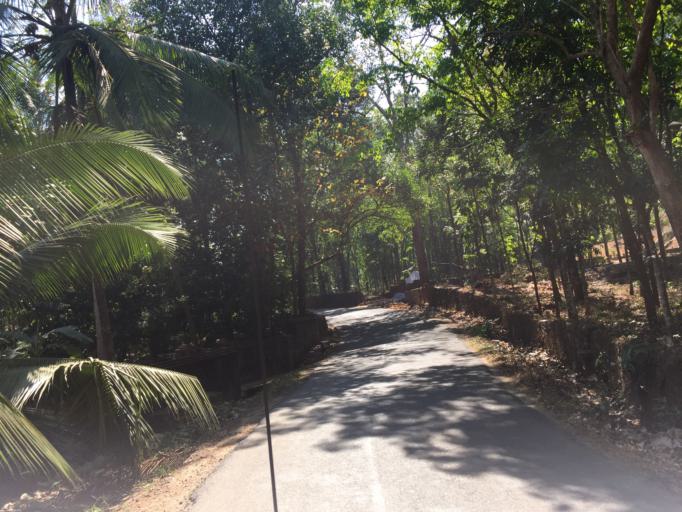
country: IN
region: Kerala
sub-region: Kottayam
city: Erattupetta
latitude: 9.6871
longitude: 76.7650
